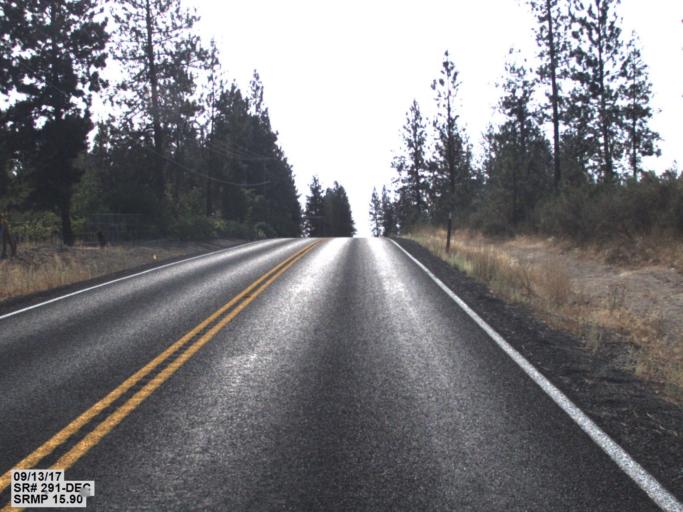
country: US
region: Washington
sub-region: Spokane County
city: Deer Park
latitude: 47.8379
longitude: -117.6066
